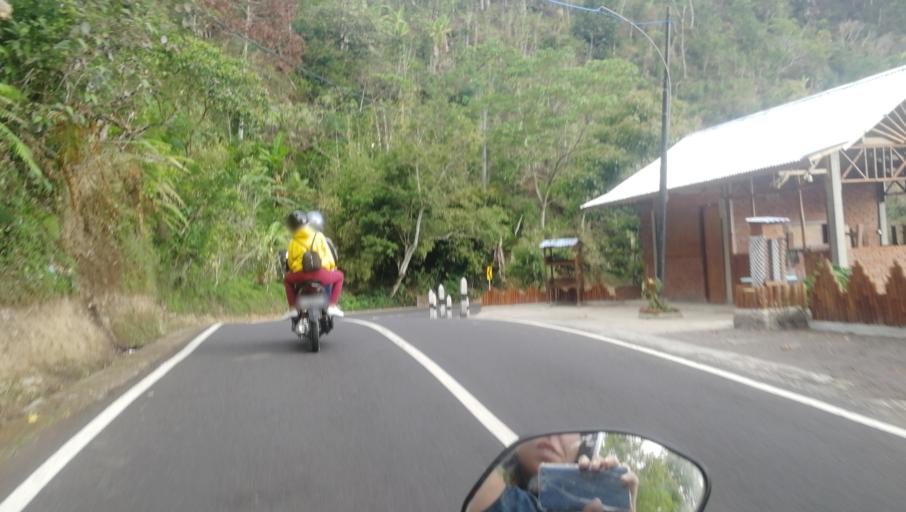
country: ID
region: Bali
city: Munduk
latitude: -8.2549
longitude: 115.0758
